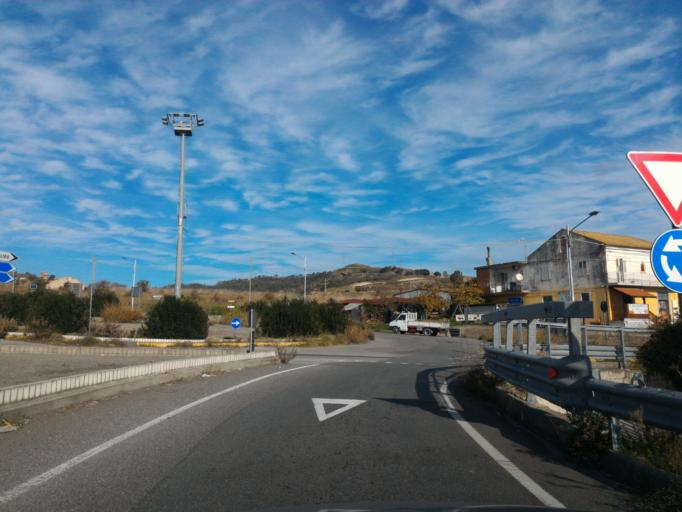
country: IT
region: Calabria
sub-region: Provincia di Catanzaro
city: Cava-Cuculera Nobile
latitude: 38.9001
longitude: 16.6356
